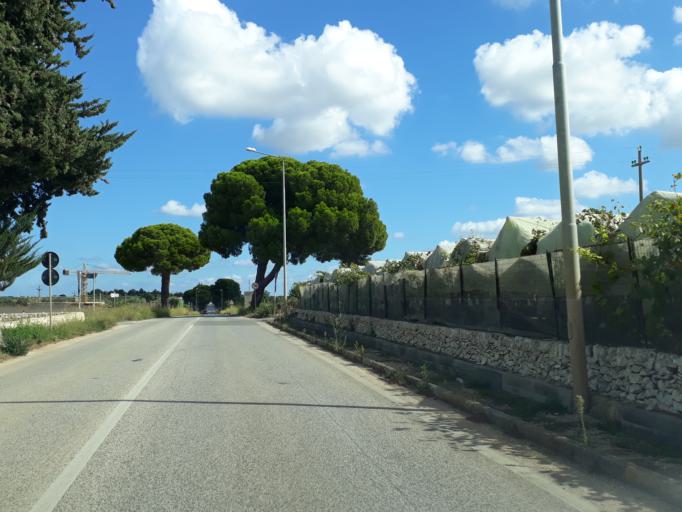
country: IT
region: Apulia
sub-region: Provincia di Bari
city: Rutigliano
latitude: 41.0180
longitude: 17.0208
